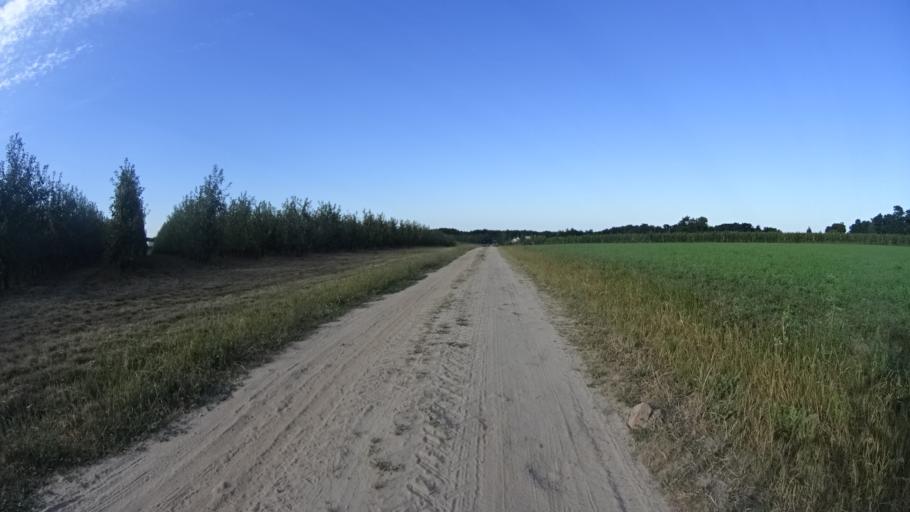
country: PL
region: Masovian Voivodeship
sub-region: Powiat grojecki
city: Goszczyn
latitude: 51.6886
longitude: 20.8125
